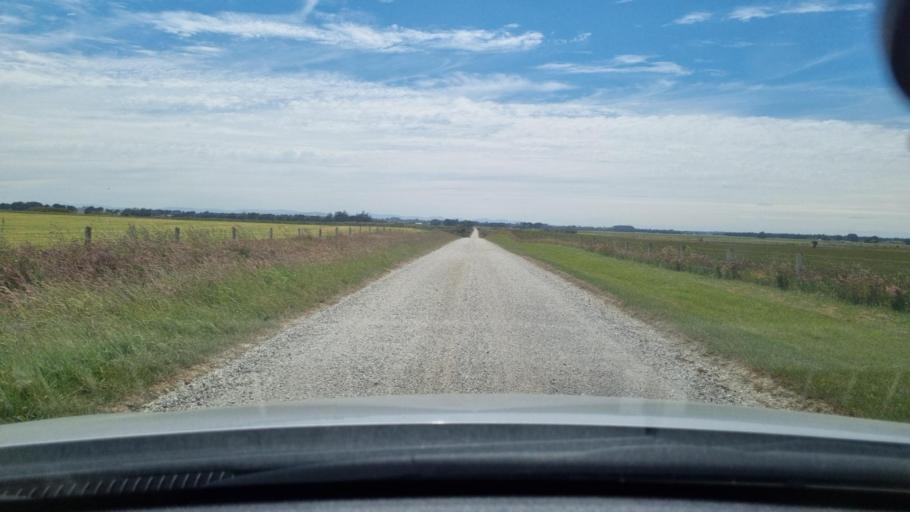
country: NZ
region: Southland
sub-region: Invercargill City
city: Invercargill
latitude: -46.3993
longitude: 168.2633
